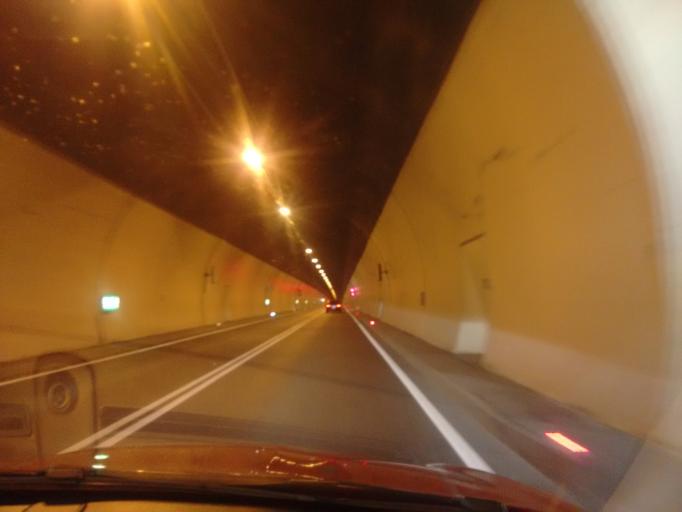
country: AT
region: Upper Austria
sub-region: Politischer Bezirk Gmunden
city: Ebensee
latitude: 47.8210
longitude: 13.7813
